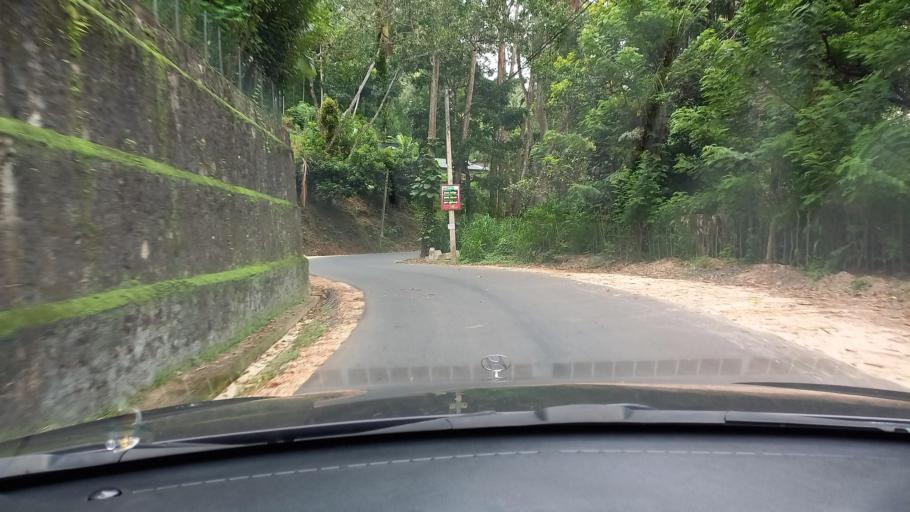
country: LK
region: Central
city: Gampola
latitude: 7.2057
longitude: 80.6288
